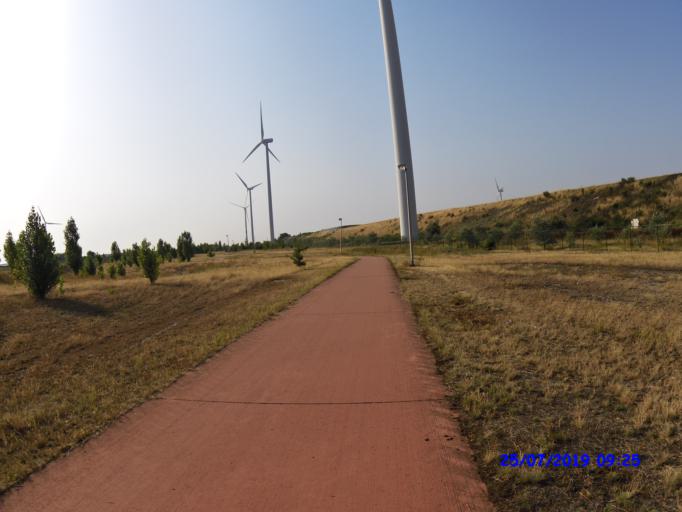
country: BE
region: Flanders
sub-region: Provincie Limburg
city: Lommel
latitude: 51.2052
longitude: 5.2570
